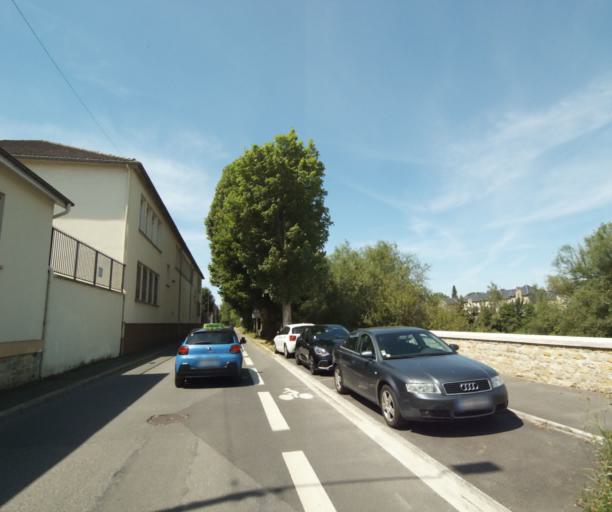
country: FR
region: Champagne-Ardenne
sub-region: Departement des Ardennes
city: Charleville-Mezieres
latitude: 49.7589
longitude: 4.7150
